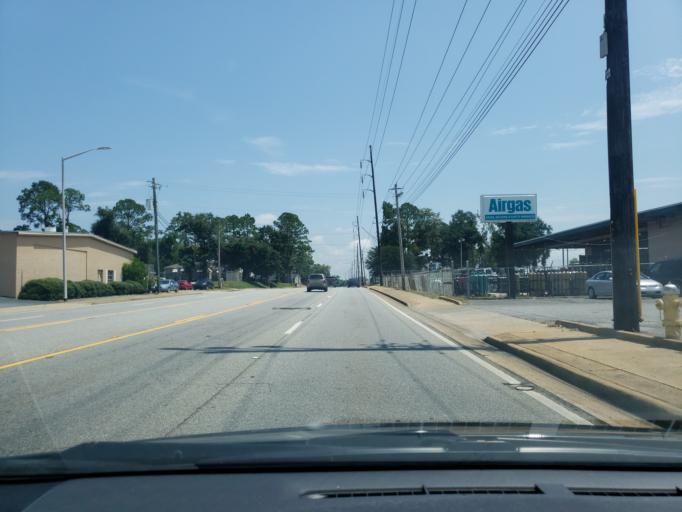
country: US
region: Georgia
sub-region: Dougherty County
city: Albany
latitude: 31.5809
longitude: -84.1864
